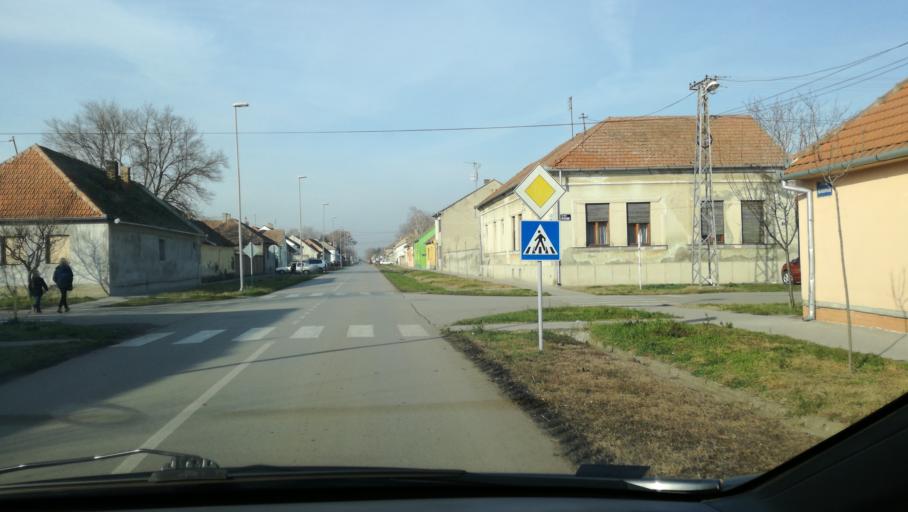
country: RS
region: Autonomna Pokrajina Vojvodina
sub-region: Severnobanatski Okrug
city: Kikinda
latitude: 45.8306
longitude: 20.4841
